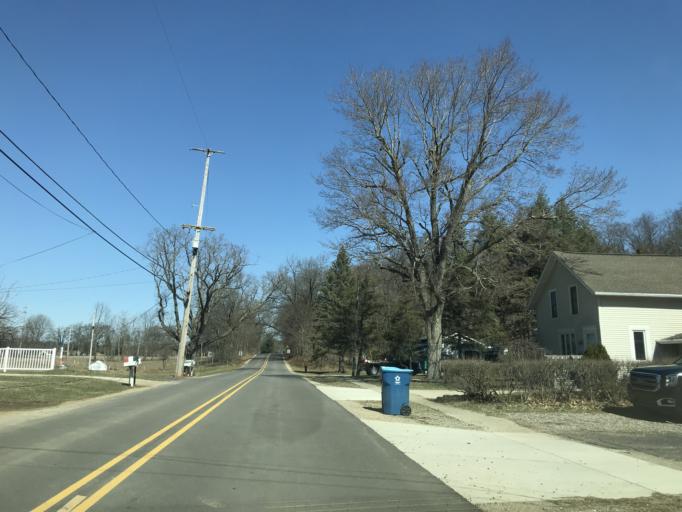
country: US
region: Michigan
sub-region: Hillsdale County
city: Jonesville
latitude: 41.9830
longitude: -84.6710
